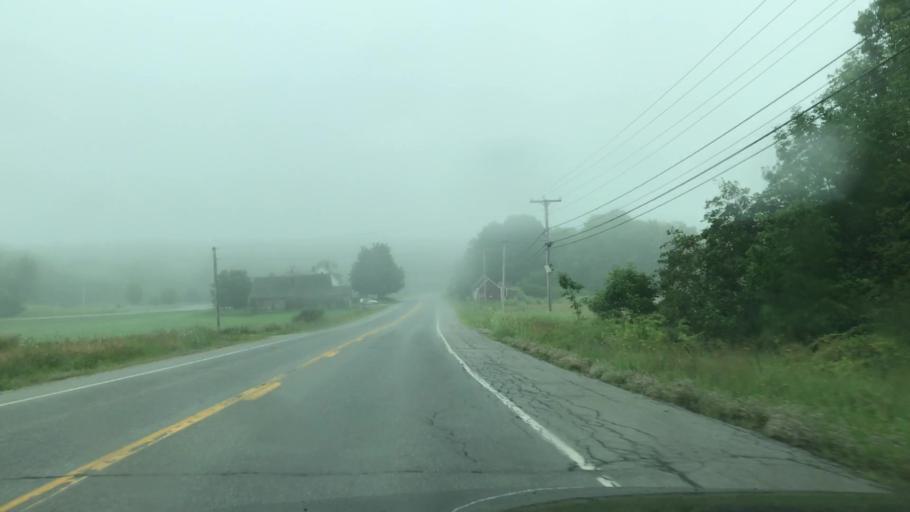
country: US
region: Maine
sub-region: Knox County
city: Rockport
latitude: 44.1867
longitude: -69.0943
